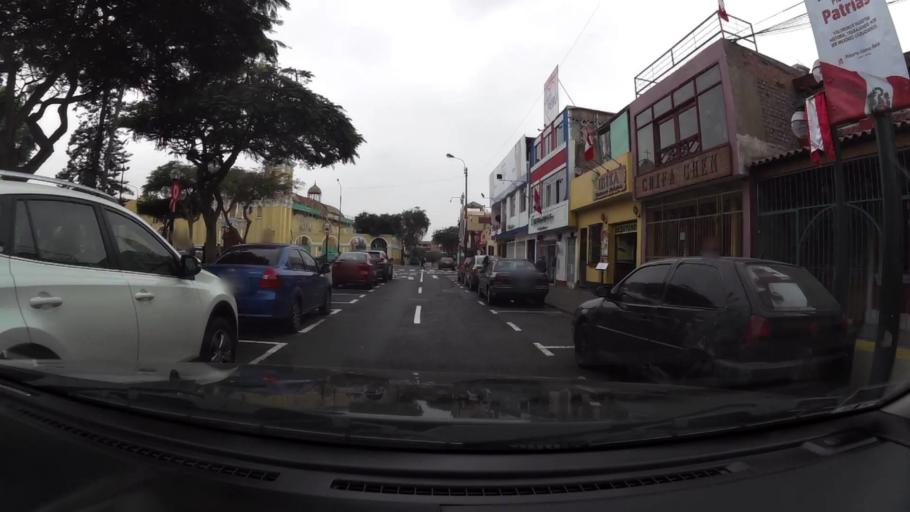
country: PE
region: Lima
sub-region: Lima
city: Surco
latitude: -12.1457
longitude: -77.0050
